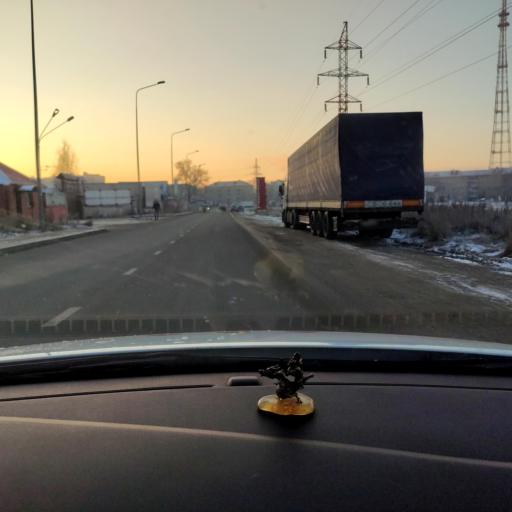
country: RU
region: Tatarstan
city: Staroye Arakchino
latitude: 55.8288
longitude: 49.0312
